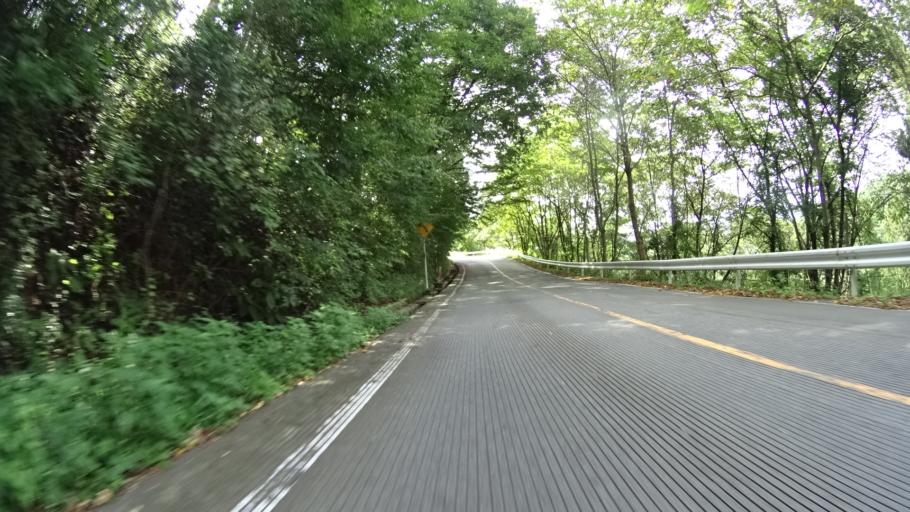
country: JP
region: Yamanashi
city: Kofu-shi
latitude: 35.7174
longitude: 138.5547
